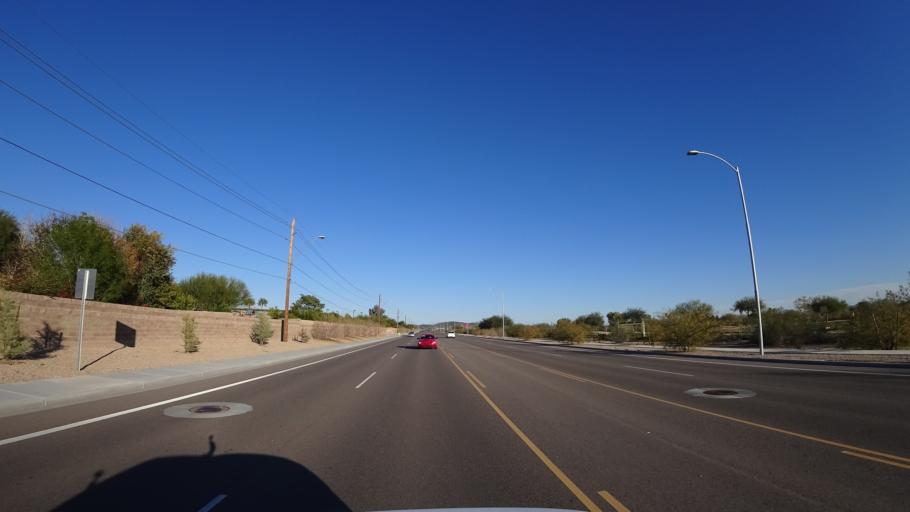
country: US
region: Arizona
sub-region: Maricopa County
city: Peoria
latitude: 33.6980
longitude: -112.1667
